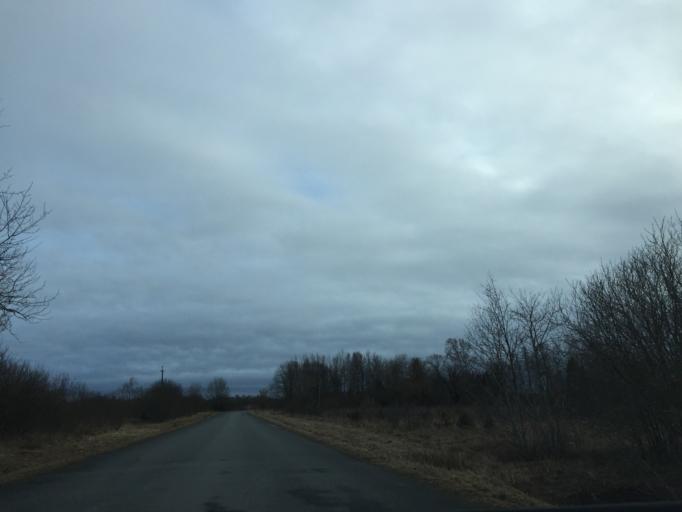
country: EE
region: Laeaene
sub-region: Haapsalu linn
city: Haapsalu
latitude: 58.8139
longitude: 23.5504
